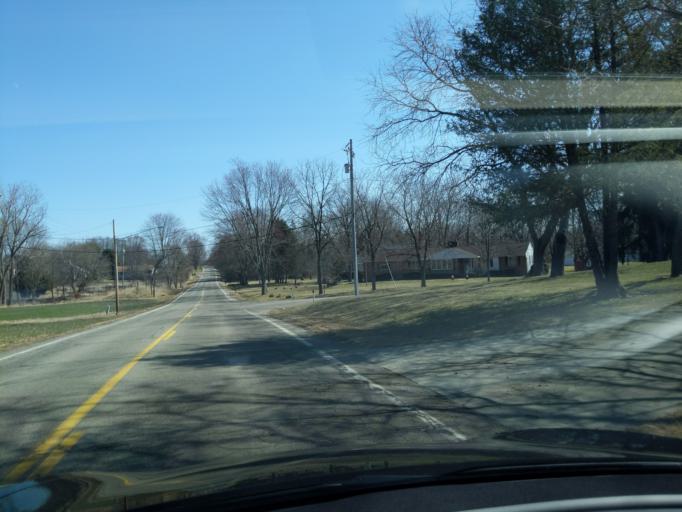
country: US
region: Michigan
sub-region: Ingham County
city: Holt
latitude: 42.6547
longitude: -84.4949
